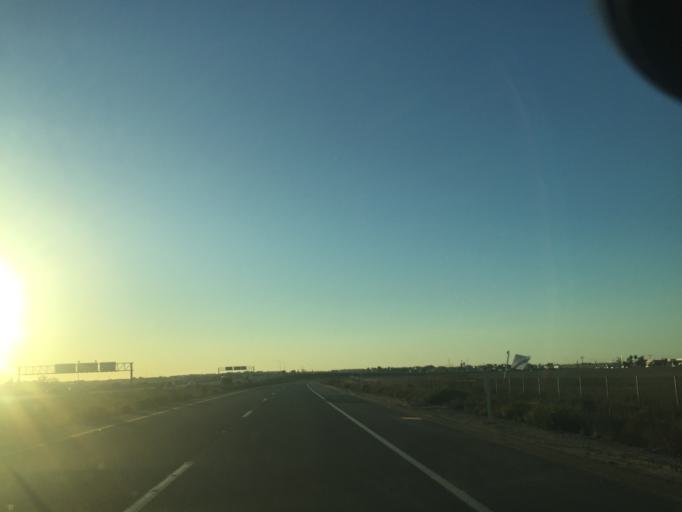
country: MX
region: Baja California
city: Tijuana
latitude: 32.5649
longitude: -116.9540
